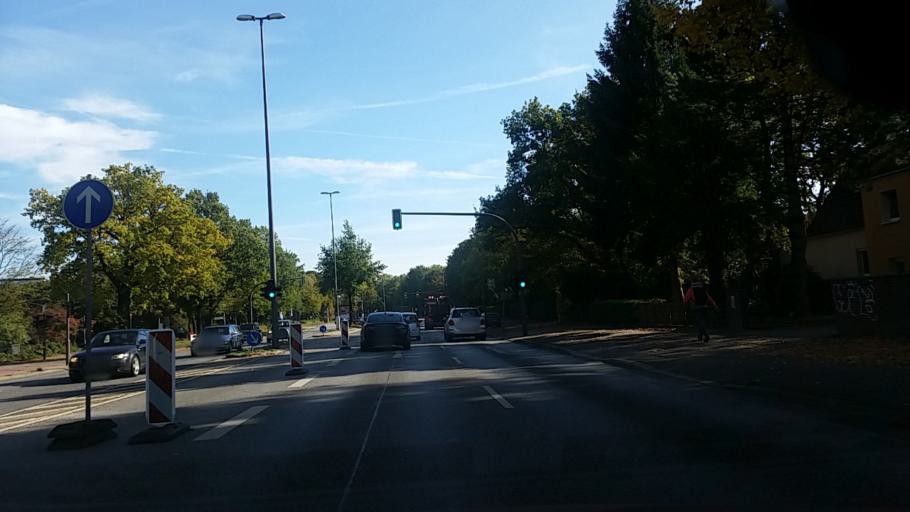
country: DE
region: Schleswig-Holstein
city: Halstenbek
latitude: 53.5744
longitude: 9.8342
